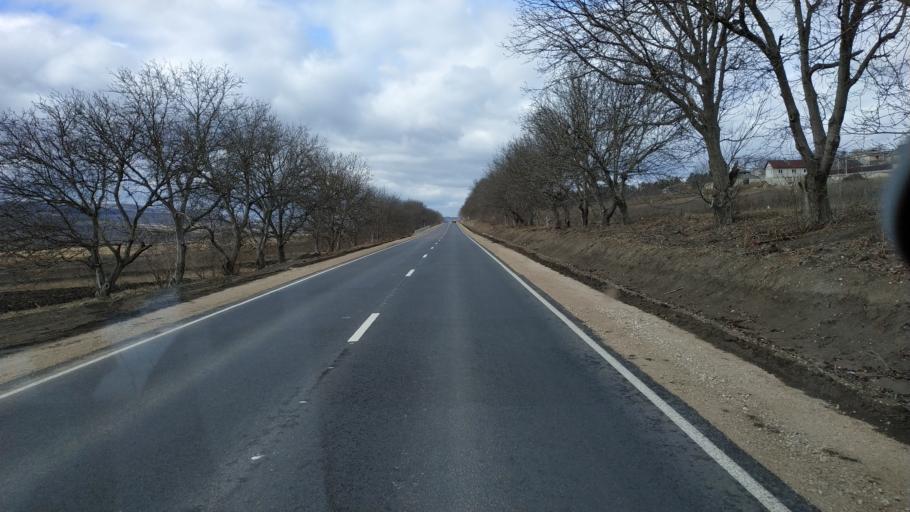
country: MD
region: Stinga Nistrului
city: Bucovat
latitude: 47.2044
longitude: 28.4254
